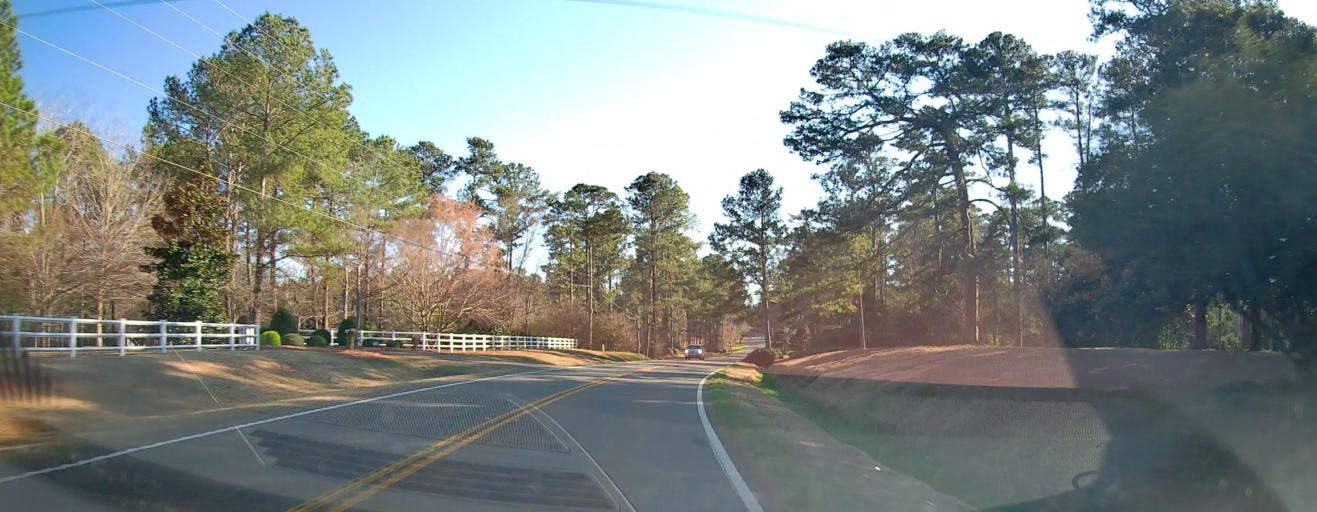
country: US
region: Georgia
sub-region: Sumter County
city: Americus
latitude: 32.0315
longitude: -84.2189
